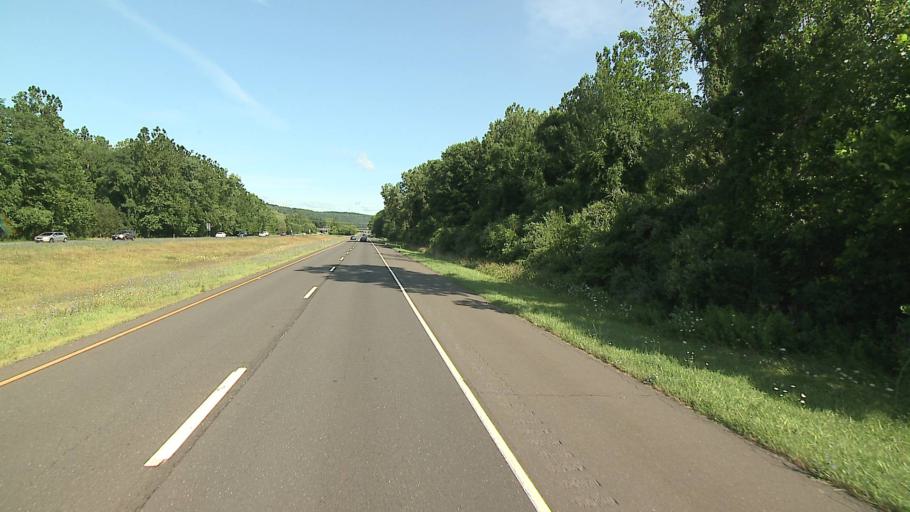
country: US
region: Connecticut
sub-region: Fairfield County
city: Danbury
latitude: 41.4630
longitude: -73.3998
